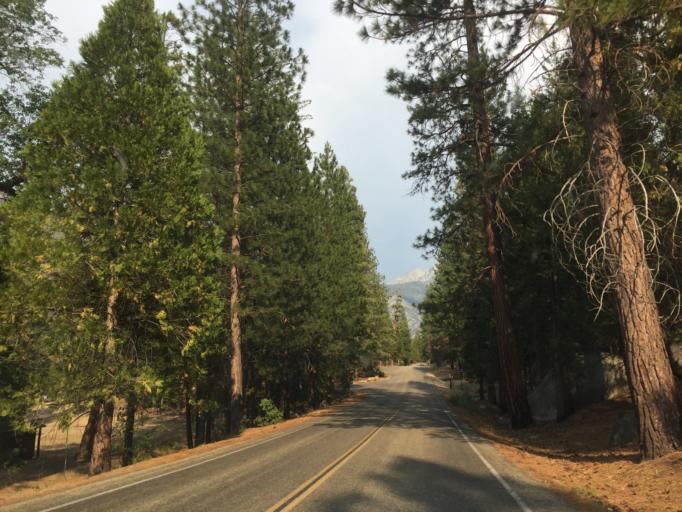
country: US
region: California
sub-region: Tulare County
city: Three Rivers
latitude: 36.7895
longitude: -118.6740
